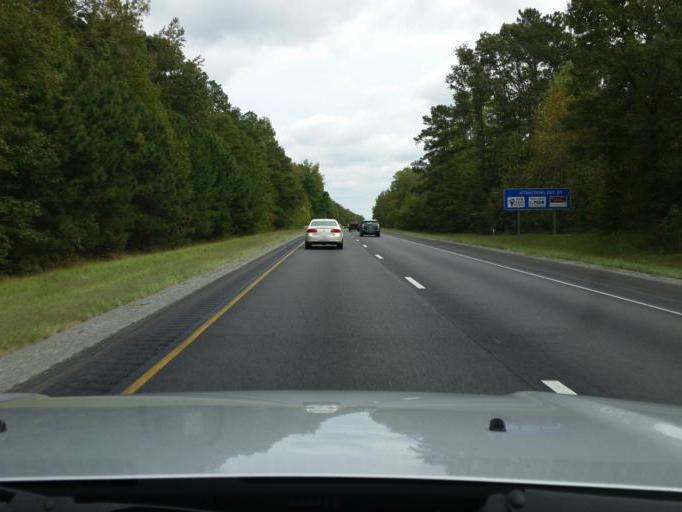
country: US
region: Virginia
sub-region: New Kent County
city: New Kent
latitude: 37.5073
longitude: -77.1046
